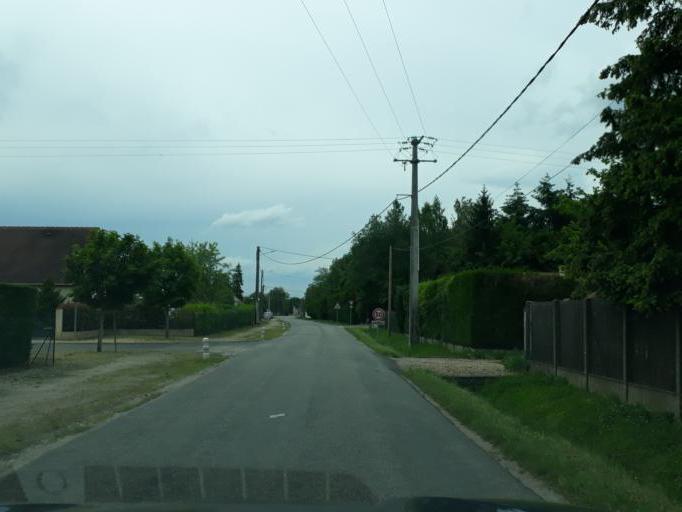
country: FR
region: Centre
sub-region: Departement du Loiret
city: Tigy
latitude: 47.7905
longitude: 2.2074
